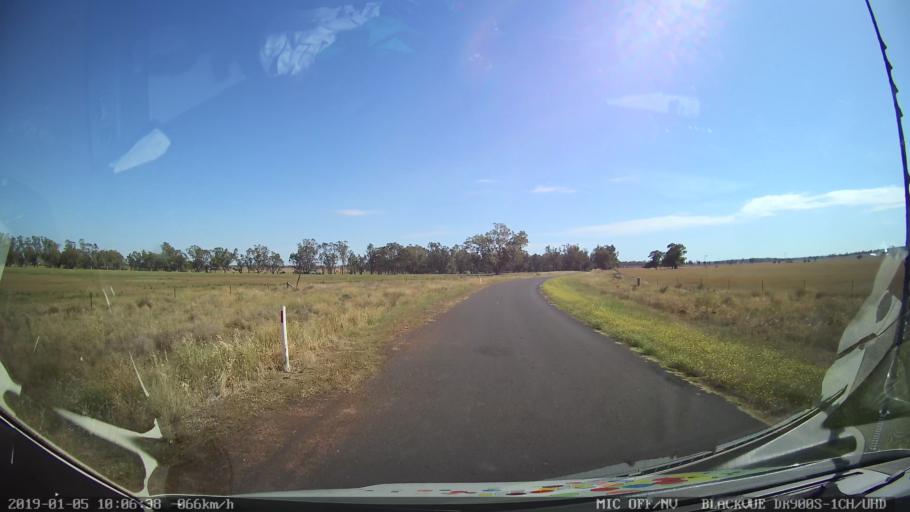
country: AU
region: New South Wales
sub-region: Gilgandra
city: Gilgandra
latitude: -31.6563
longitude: 148.8701
